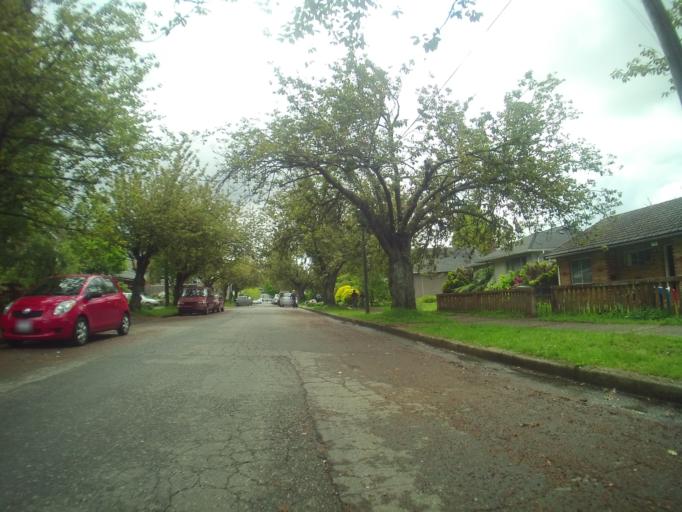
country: CA
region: British Columbia
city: Vancouver
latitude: 49.2555
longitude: -123.0728
